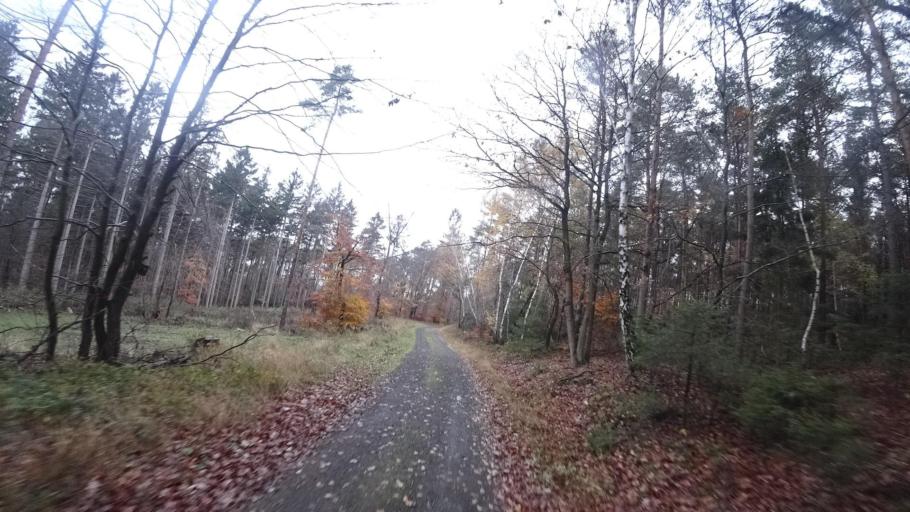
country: DE
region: Rheinland-Pfalz
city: Schalkenbach
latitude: 50.5178
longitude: 7.1293
